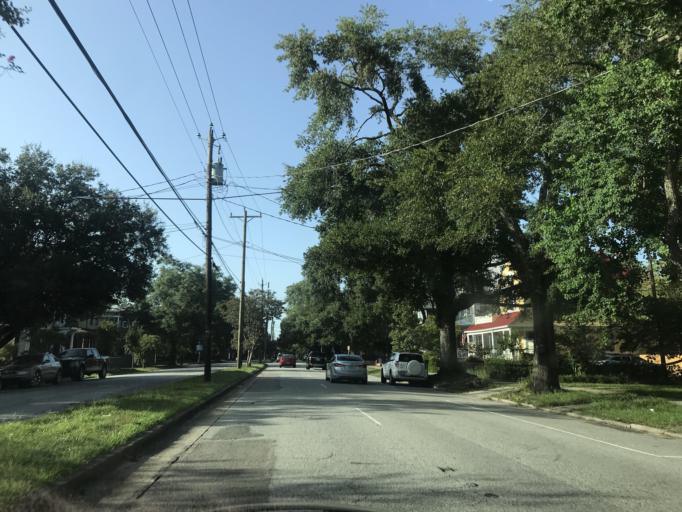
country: US
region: North Carolina
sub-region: New Hanover County
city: Wilmington
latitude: 34.2297
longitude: -77.9453
